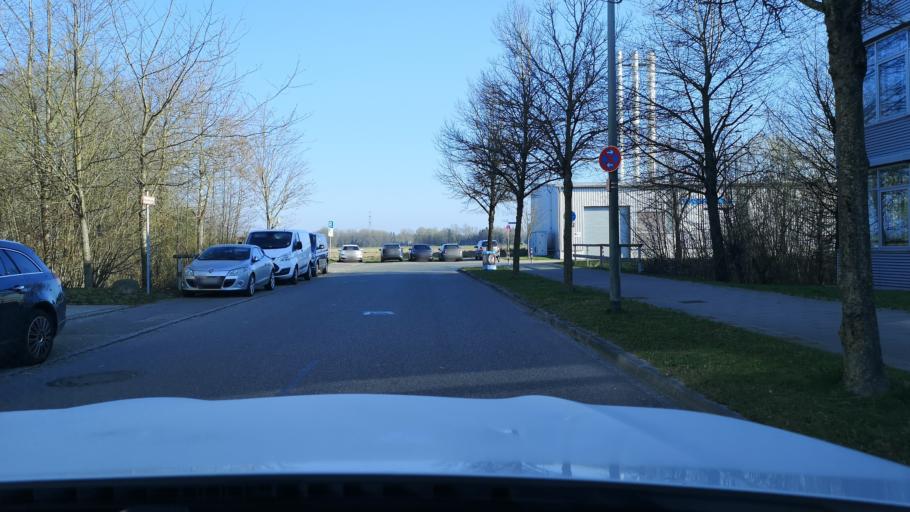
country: DE
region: Bavaria
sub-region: Upper Bavaria
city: Markt Schwaben
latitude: 48.1948
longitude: 11.8537
